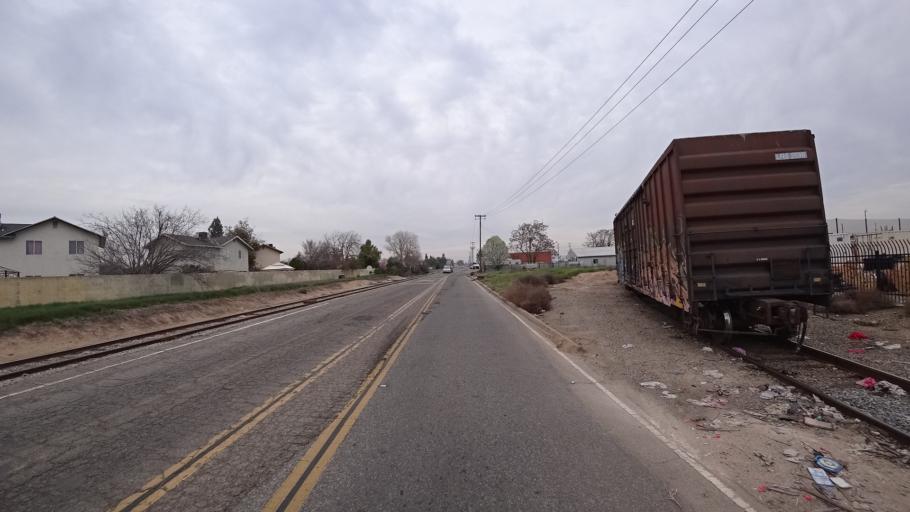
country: US
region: California
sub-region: Fresno County
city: Fresno
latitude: 36.7213
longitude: -119.7600
